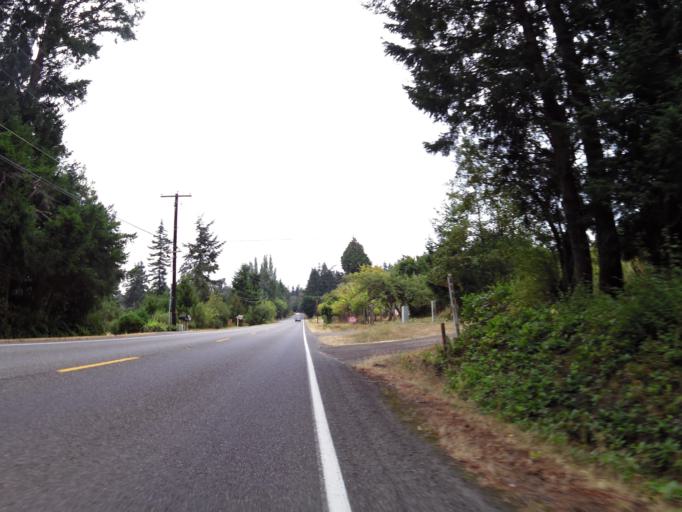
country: US
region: Washington
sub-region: Jefferson County
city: Port Hadlock-Irondale
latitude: 47.9927
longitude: -122.7226
